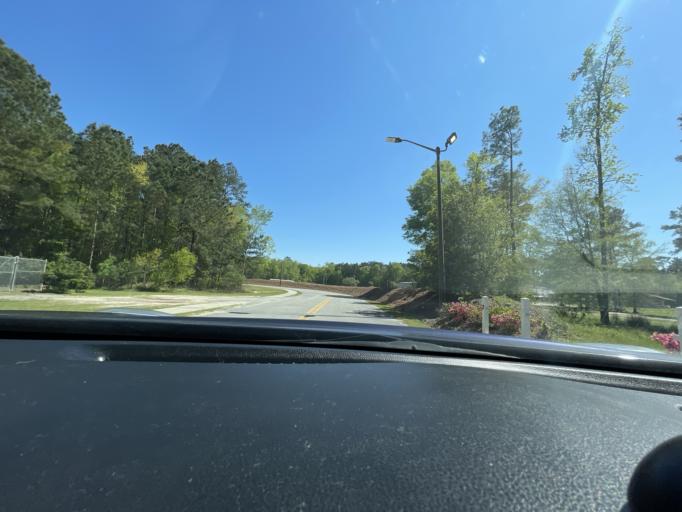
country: US
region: Georgia
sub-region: Chatham County
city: Pooler
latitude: 32.1318
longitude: -81.2628
